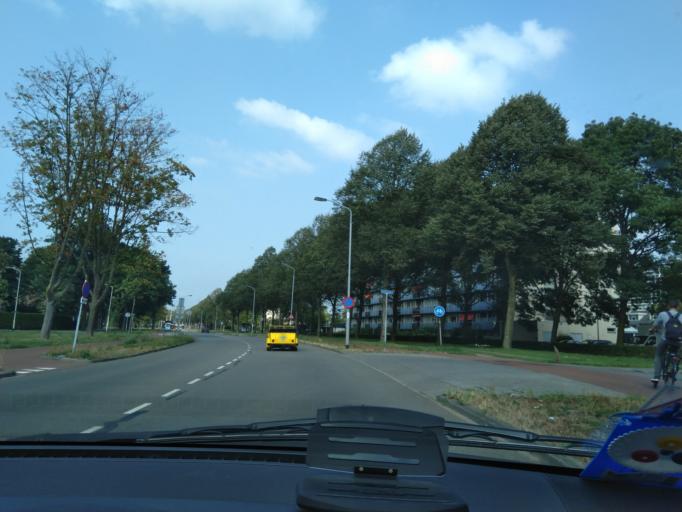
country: NL
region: North Brabant
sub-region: Gemeente Breda
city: Hoge Vucht
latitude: 51.5844
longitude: 4.8196
